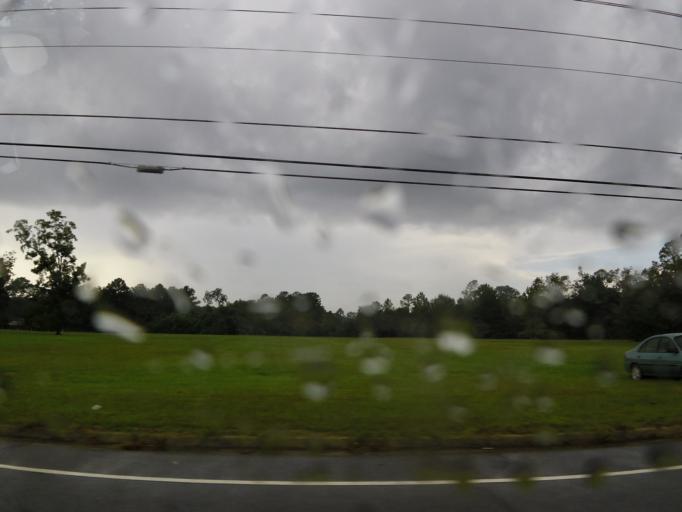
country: US
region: Georgia
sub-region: Wayne County
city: Jesup
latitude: 31.5889
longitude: -81.8740
